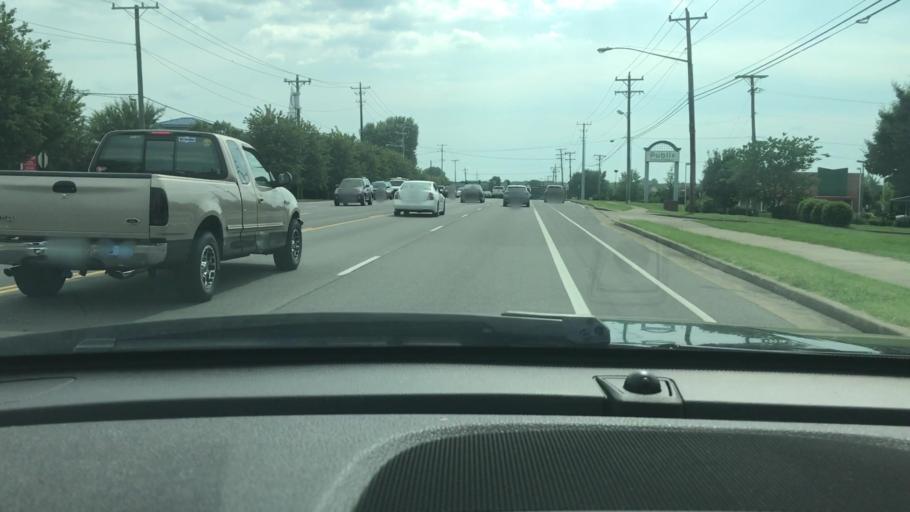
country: US
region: Tennessee
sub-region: Sumner County
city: Hendersonville
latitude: 36.3094
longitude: -86.6024
